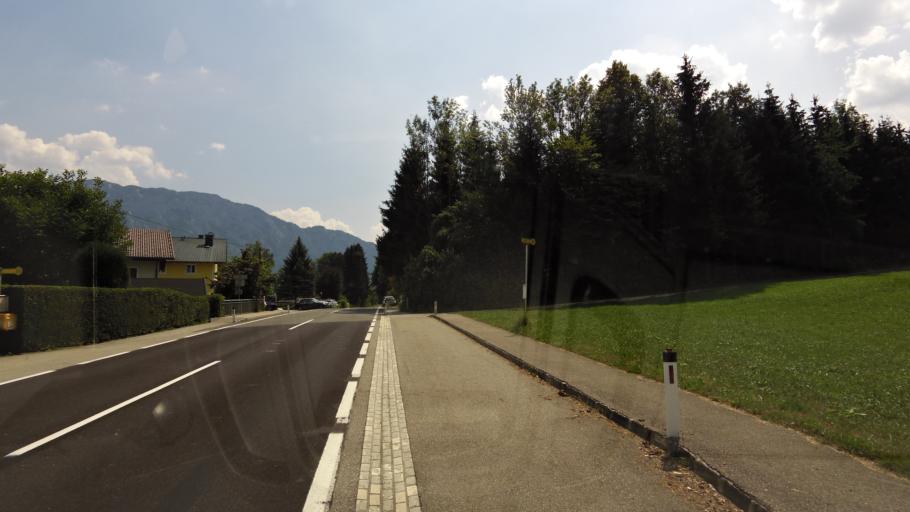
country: AT
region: Upper Austria
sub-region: Politischer Bezirk Vocklabruck
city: Steinbach am Attersee
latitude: 47.8405
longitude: 13.5219
